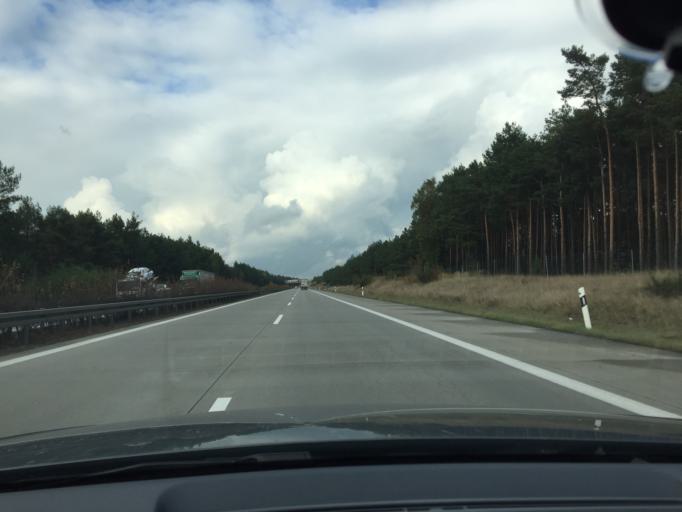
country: DE
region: Brandenburg
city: Teupitz
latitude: 52.1001
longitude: 13.6475
